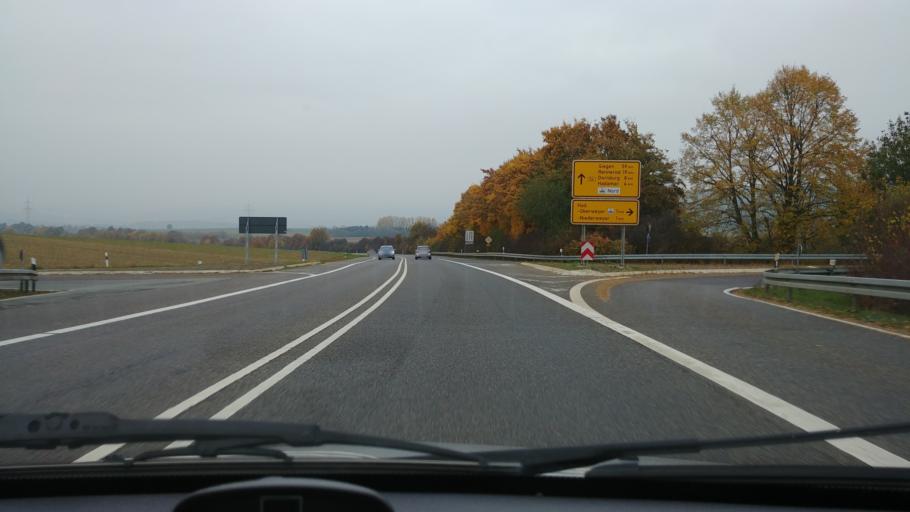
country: DE
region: Hesse
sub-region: Regierungsbezirk Giessen
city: Dehrn
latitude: 50.4538
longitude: 8.0857
